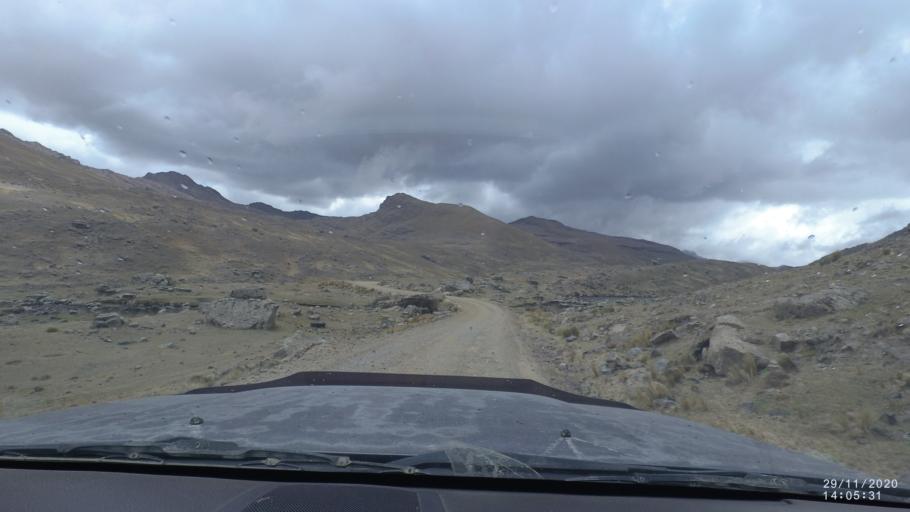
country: BO
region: Cochabamba
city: Sipe Sipe
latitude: -17.2073
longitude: -66.3769
